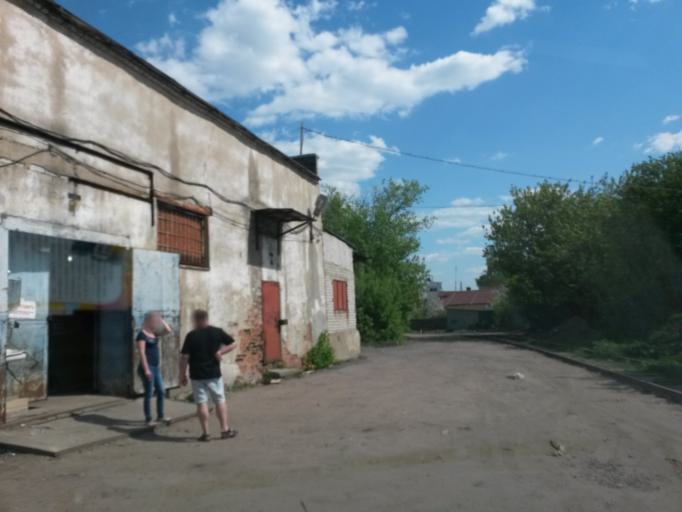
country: RU
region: Jaroslavl
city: Yaroslavl
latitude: 57.6030
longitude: 39.8887
